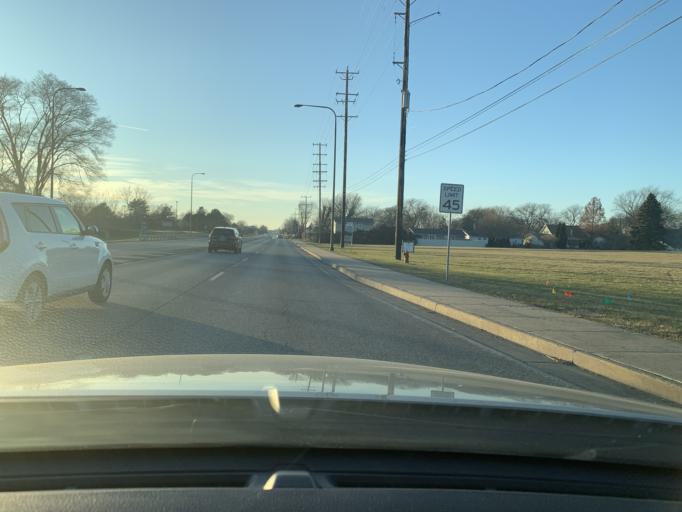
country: US
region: Illinois
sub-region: DuPage County
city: Itasca
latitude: 41.9927
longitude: -88.0037
